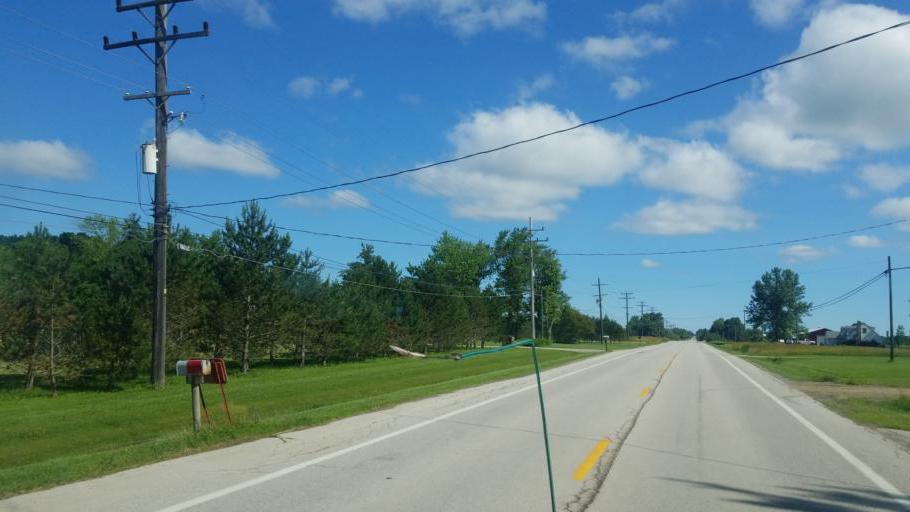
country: US
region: Ohio
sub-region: Ashtabula County
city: Conneaut
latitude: 41.8504
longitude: -80.5725
